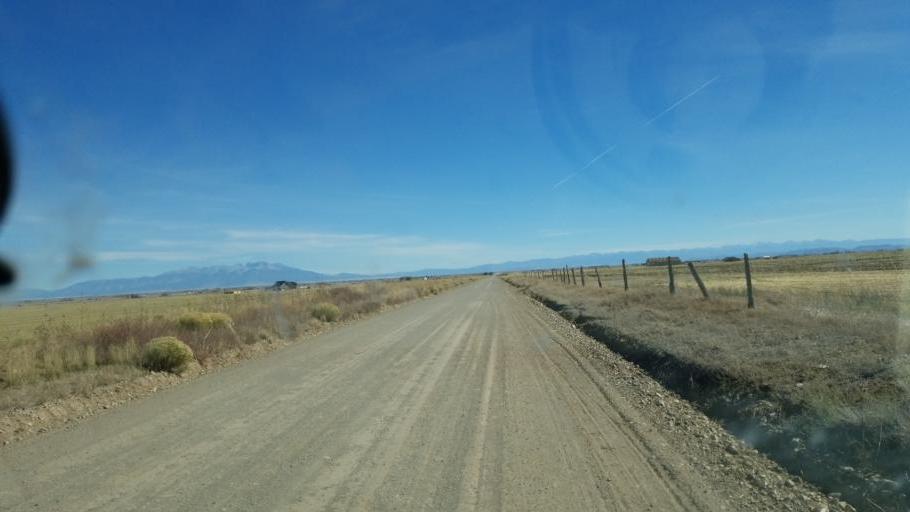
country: US
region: Colorado
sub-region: Rio Grande County
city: Monte Vista
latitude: 37.4011
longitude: -106.1270
